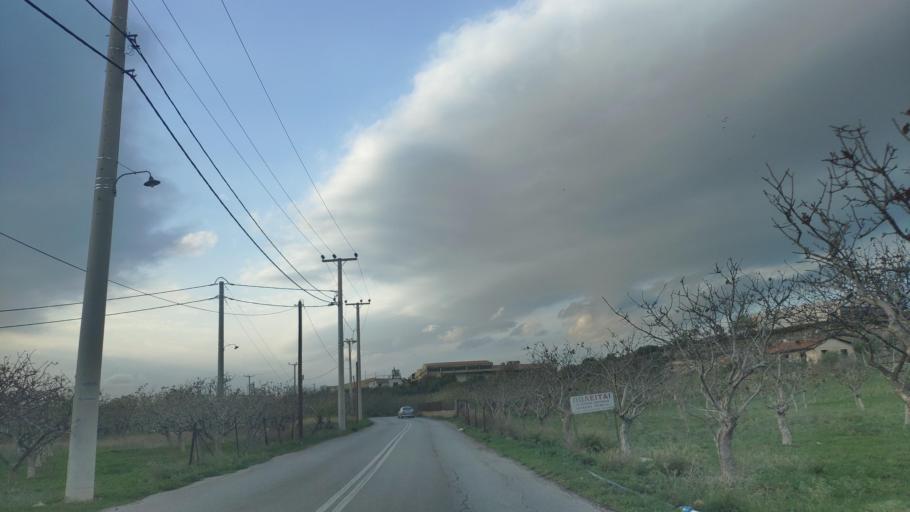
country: GR
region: Attica
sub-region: Nomarchia Dytikis Attikis
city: Nea Peramos
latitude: 37.9951
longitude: 23.3946
